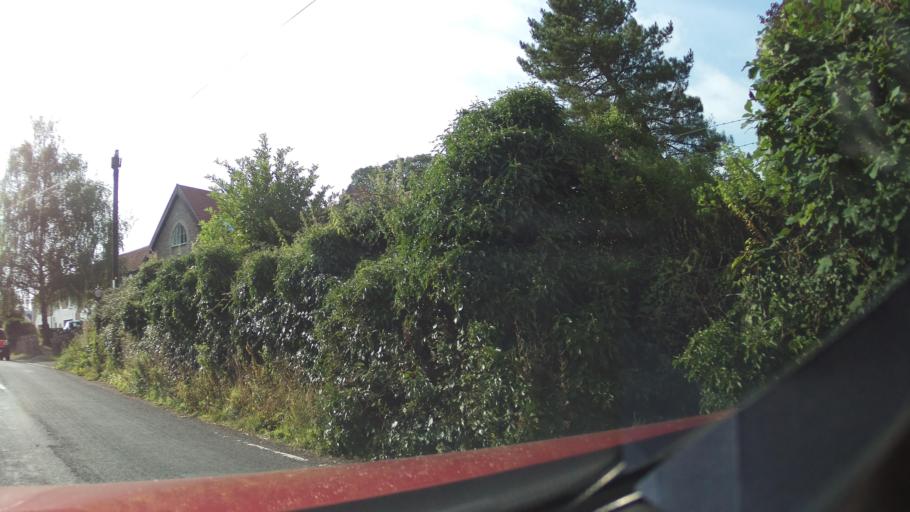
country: GB
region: England
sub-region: Bath and North East Somerset
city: Cameley
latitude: 51.2774
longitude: -2.5794
